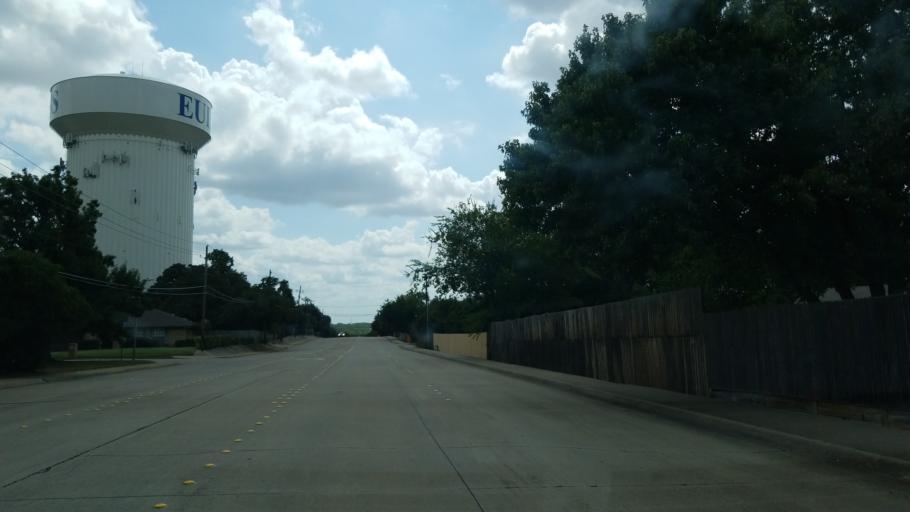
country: US
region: Texas
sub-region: Tarrant County
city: Euless
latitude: 32.8790
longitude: -97.0826
